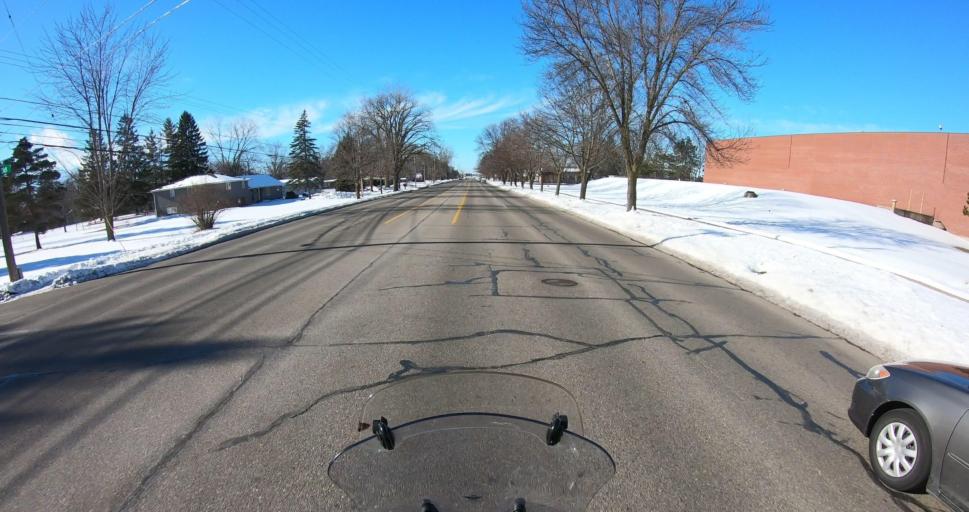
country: US
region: Michigan
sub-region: Midland County
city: Midland
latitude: 43.6048
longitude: -84.1945
